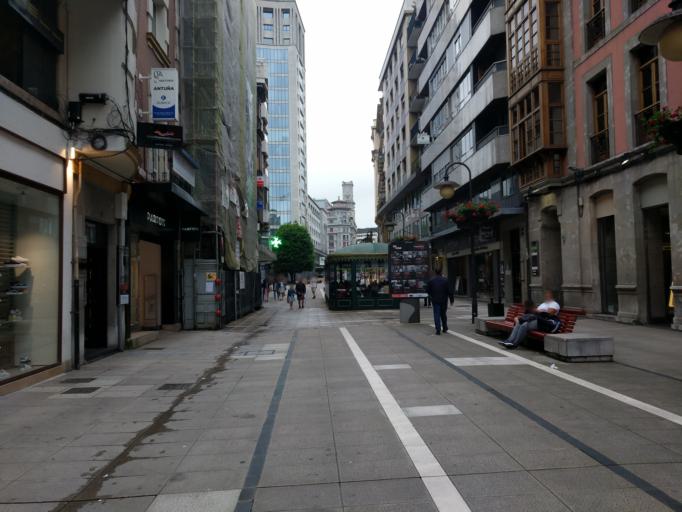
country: ES
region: Asturias
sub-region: Province of Asturias
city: Oviedo
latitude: 43.3642
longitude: -5.8496
